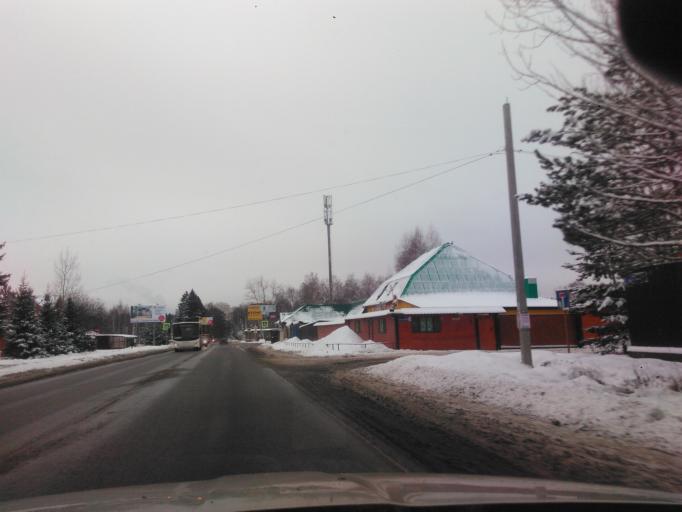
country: RU
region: Moskovskaya
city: Andreyevka
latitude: 55.9810
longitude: 37.1232
